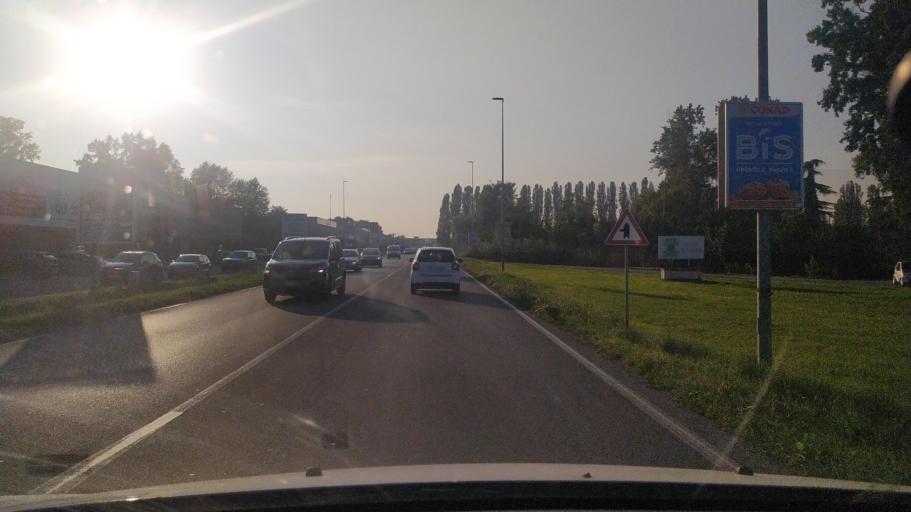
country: IT
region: Lombardy
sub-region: Provincia di Cremona
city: Capergnanica
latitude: 45.3596
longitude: 9.6505
